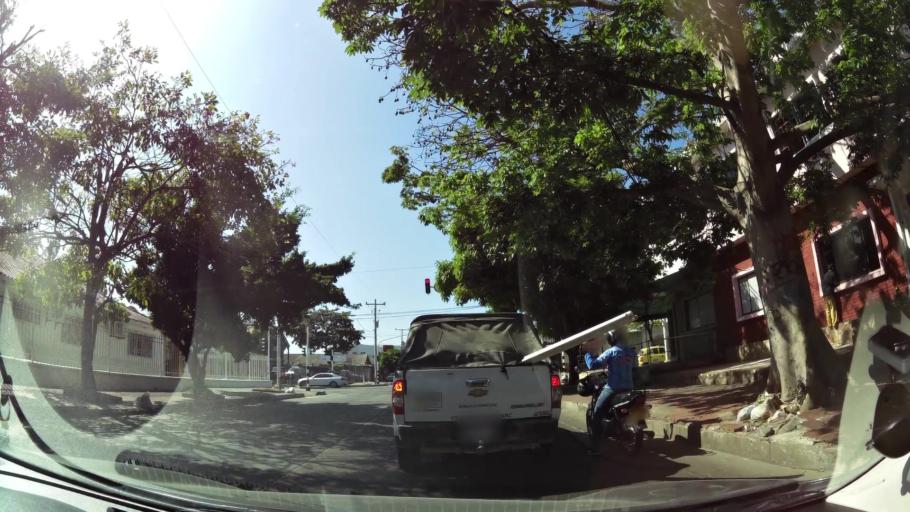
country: CO
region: Atlantico
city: Barranquilla
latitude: 10.9922
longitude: -74.8012
